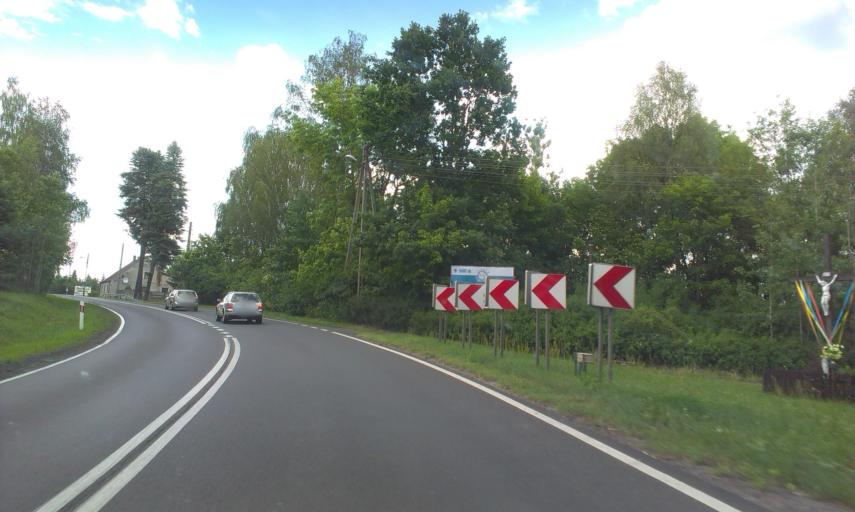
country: PL
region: Greater Poland Voivodeship
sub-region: Powiat zlotowski
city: Tarnowka
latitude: 53.3046
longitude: 16.7934
